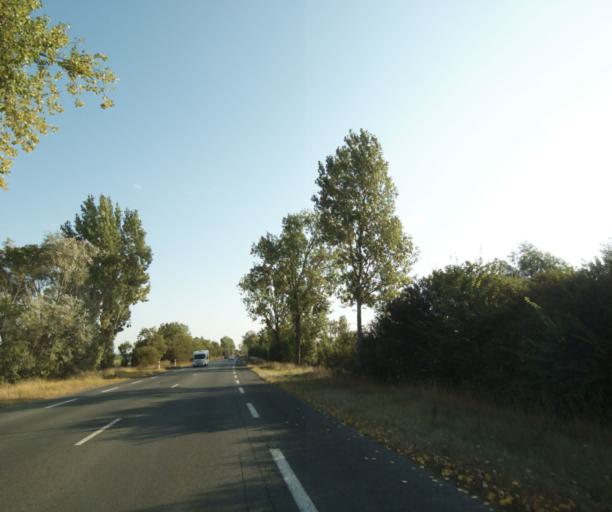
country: FR
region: Poitou-Charentes
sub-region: Departement de la Charente-Maritime
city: Saint-Hippolyte
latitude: 45.9228
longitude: -0.8830
